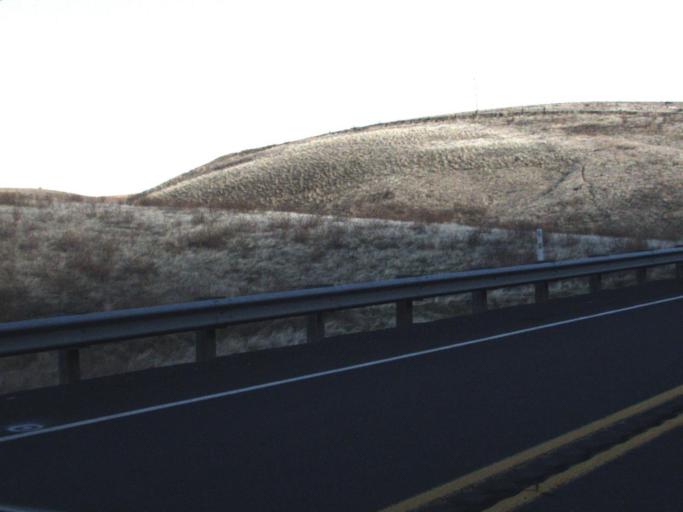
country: US
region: Washington
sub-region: Garfield County
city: Pomeroy
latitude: 46.6755
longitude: -117.8147
